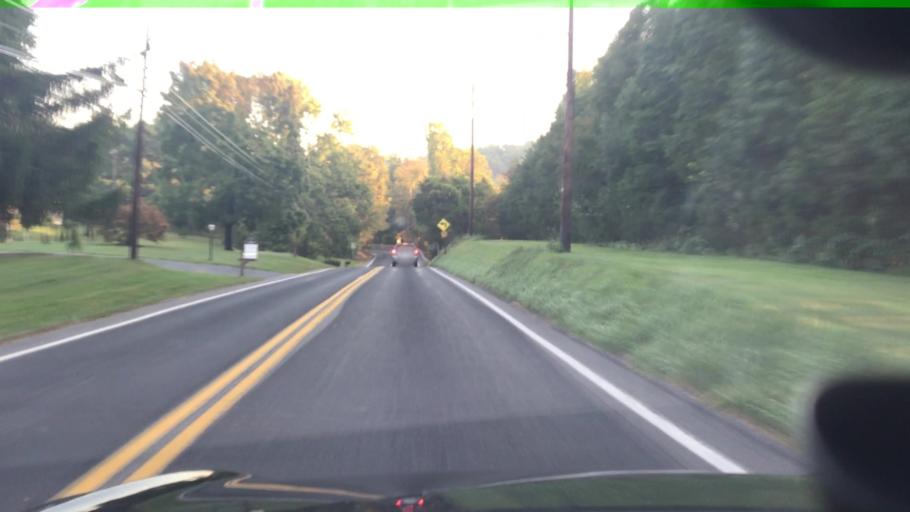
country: US
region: Pennsylvania
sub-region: Cumberland County
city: Lower Allen
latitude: 40.1714
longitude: -76.9207
